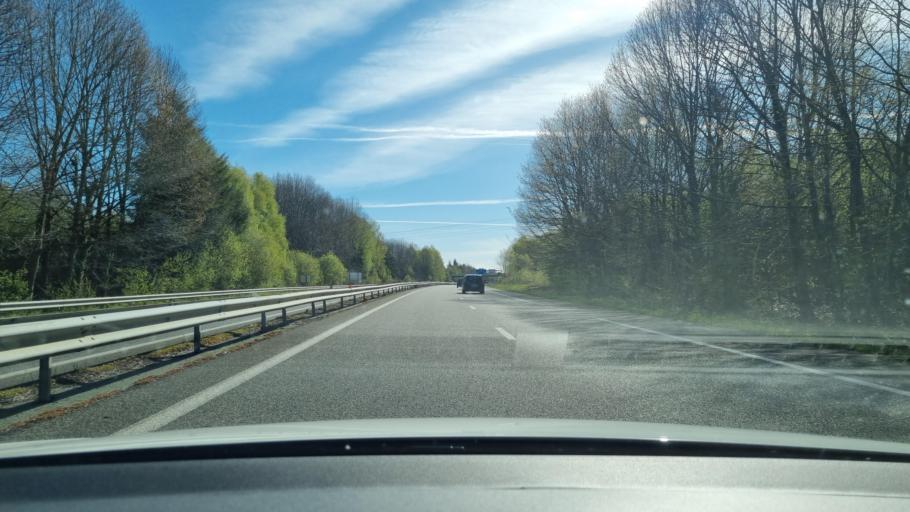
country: FR
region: Midi-Pyrenees
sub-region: Departement des Hautes-Pyrenees
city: La Barthe-de-Neste
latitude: 43.1011
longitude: 0.3826
